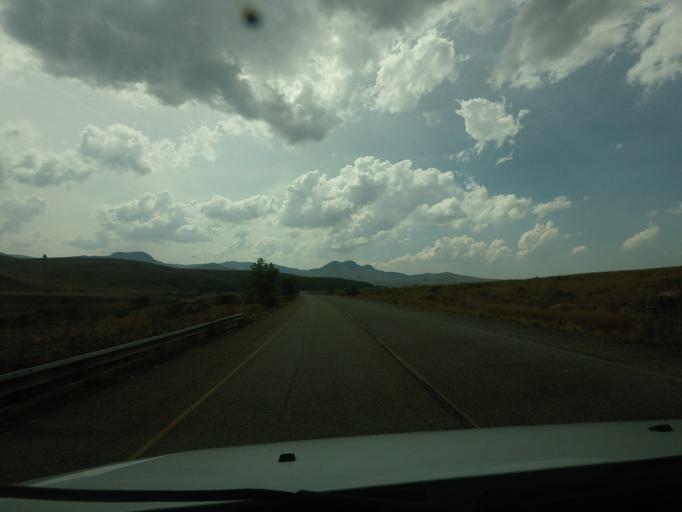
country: ZA
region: Mpumalanga
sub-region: Ehlanzeni District
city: Graksop
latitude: -24.6961
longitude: 30.8187
